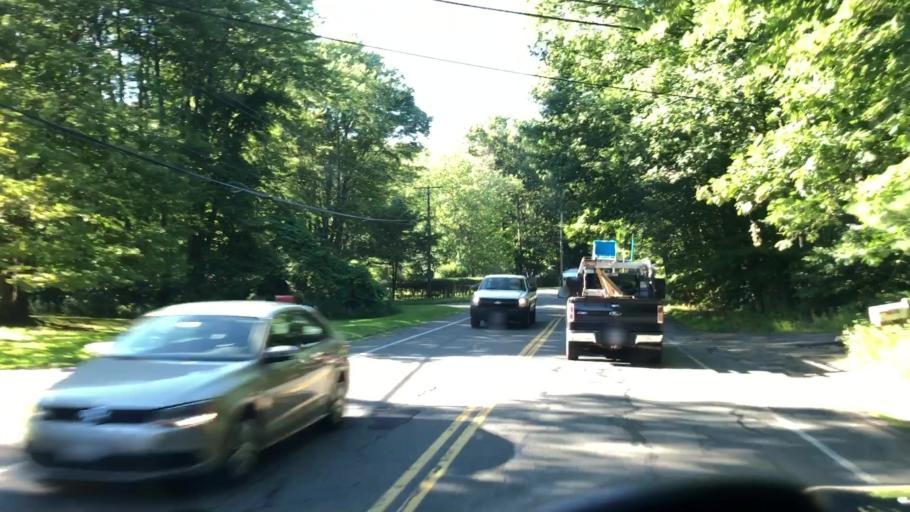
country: US
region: Massachusetts
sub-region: Hampshire County
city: Easthampton
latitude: 42.3043
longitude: -72.6752
